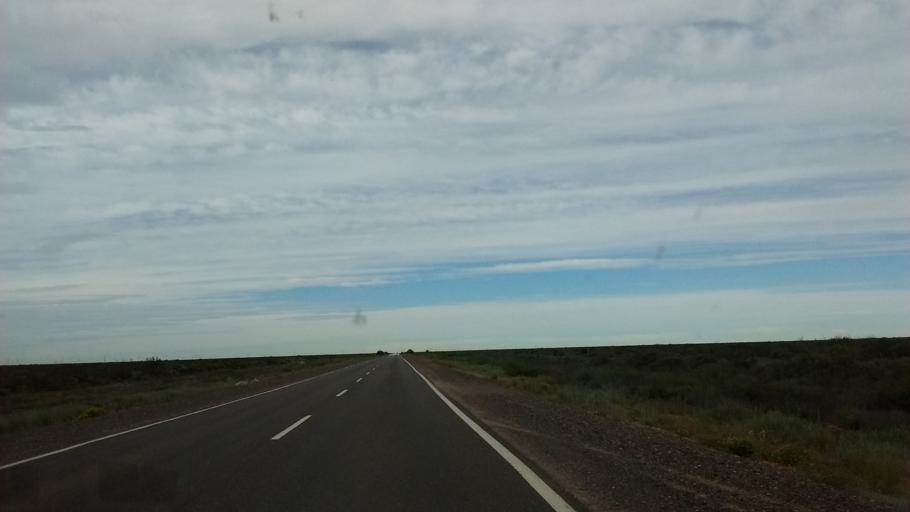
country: AR
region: Rio Negro
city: Contraalmirante Cordero
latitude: -38.5142
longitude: -68.0700
